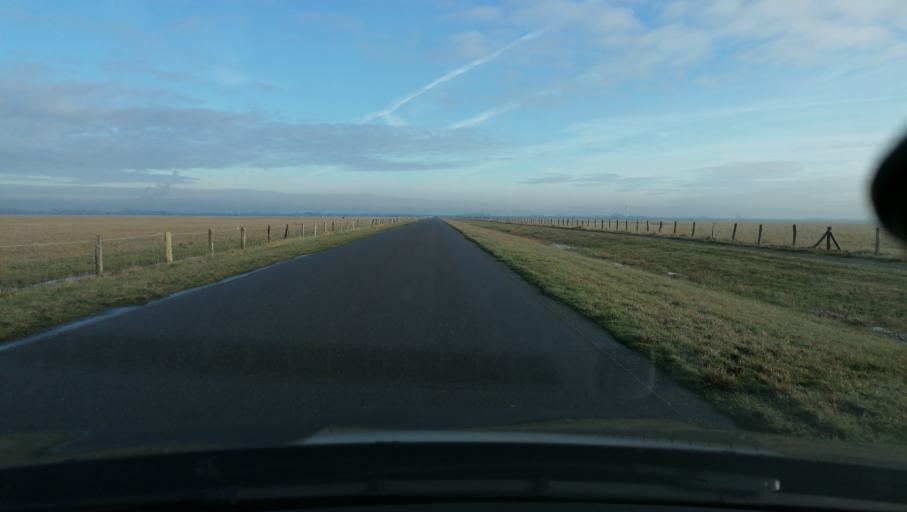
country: DE
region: Schleswig-Holstein
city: Friedrichsgabekoog
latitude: 54.1166
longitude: 8.9548
